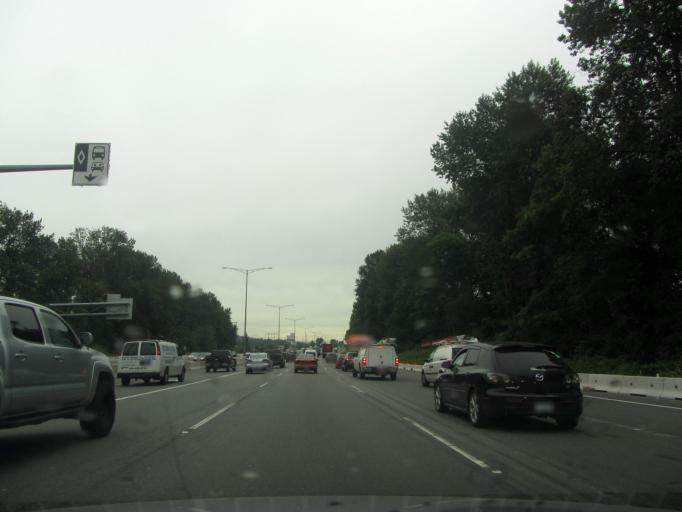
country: CA
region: British Columbia
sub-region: Fraser Valley Regional District
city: North Vancouver
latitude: 49.2639
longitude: -123.0258
